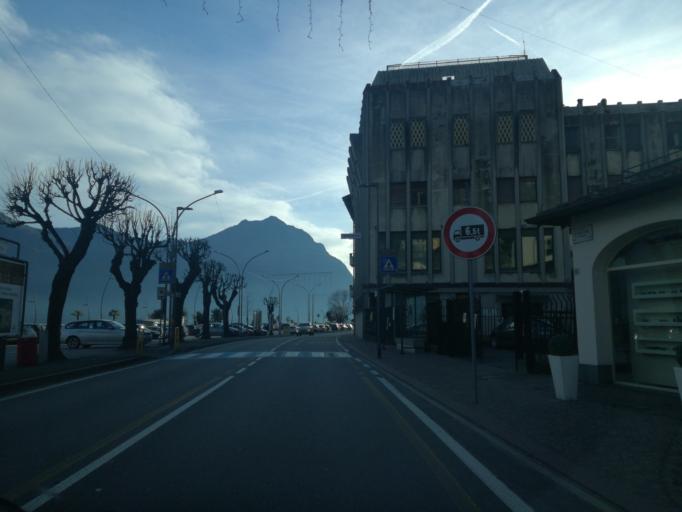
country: IT
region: Lombardy
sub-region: Provincia di Bergamo
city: Lovere
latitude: 45.8210
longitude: 10.0793
